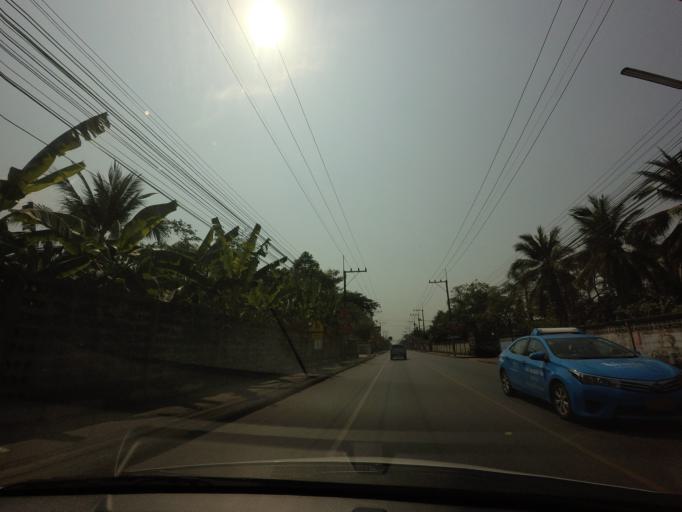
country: TH
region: Nakhon Pathom
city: Sam Phran
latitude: 13.7140
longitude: 100.2599
